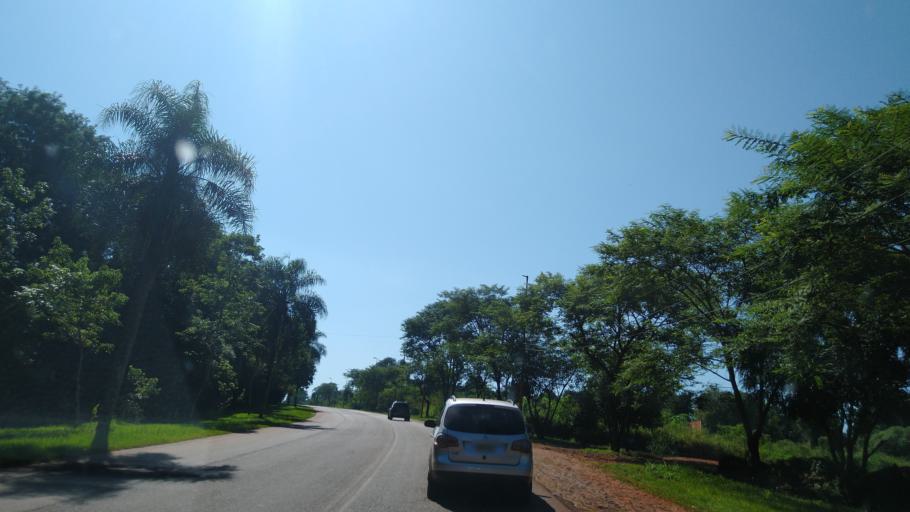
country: AR
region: Misiones
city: Puerto Esperanza
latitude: -26.0221
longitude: -54.6000
